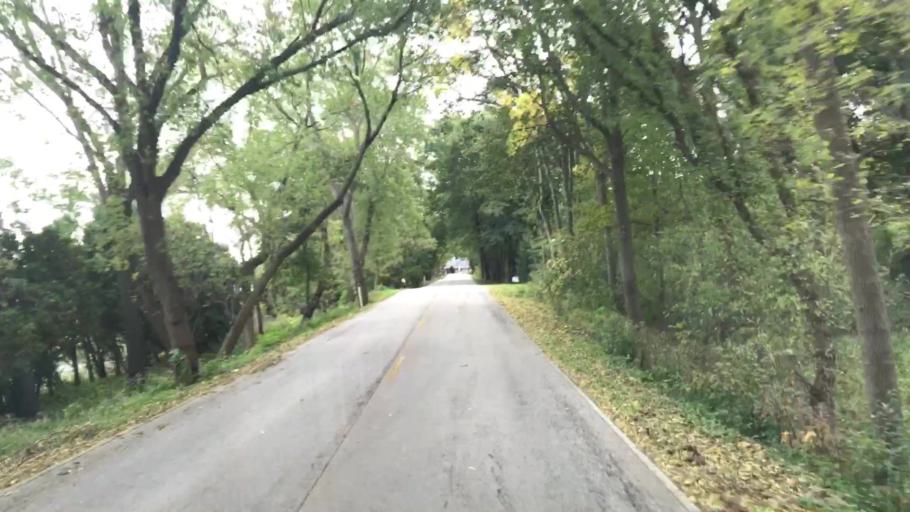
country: US
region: Wisconsin
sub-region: Waukesha County
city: Elm Grove
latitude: 43.0445
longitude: -88.0829
